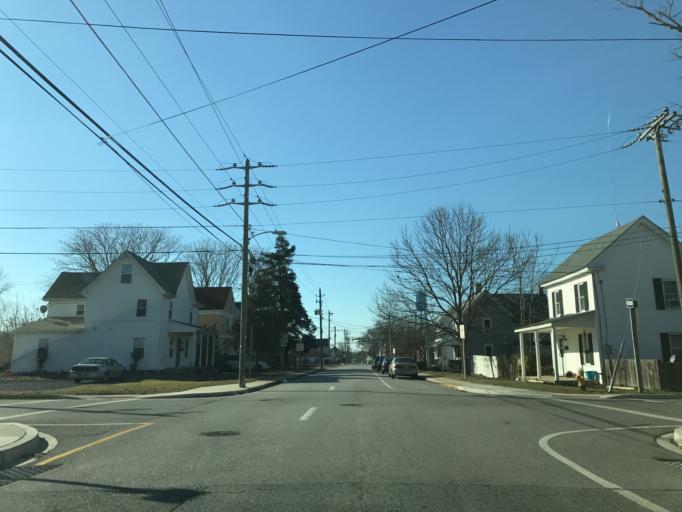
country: US
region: Maryland
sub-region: Caroline County
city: Denton
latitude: 38.8855
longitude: -75.8250
